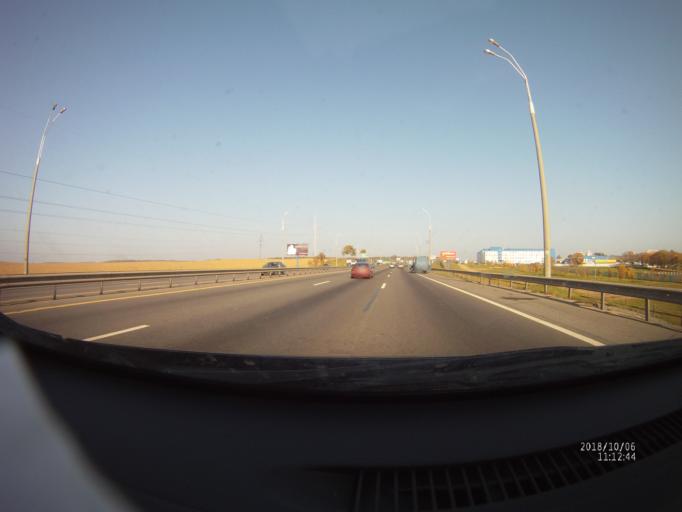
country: BY
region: Minsk
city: Novoye Medvezhino
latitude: 53.8988
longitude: 27.4088
